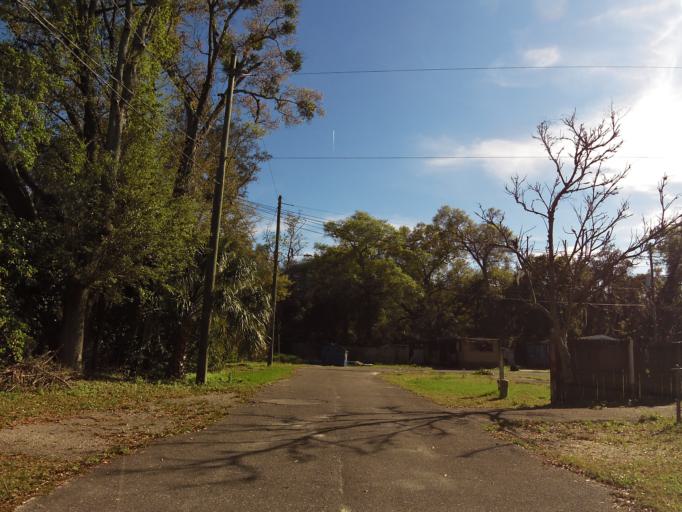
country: US
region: Florida
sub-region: Duval County
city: Jacksonville
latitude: 30.3694
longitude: -81.6498
